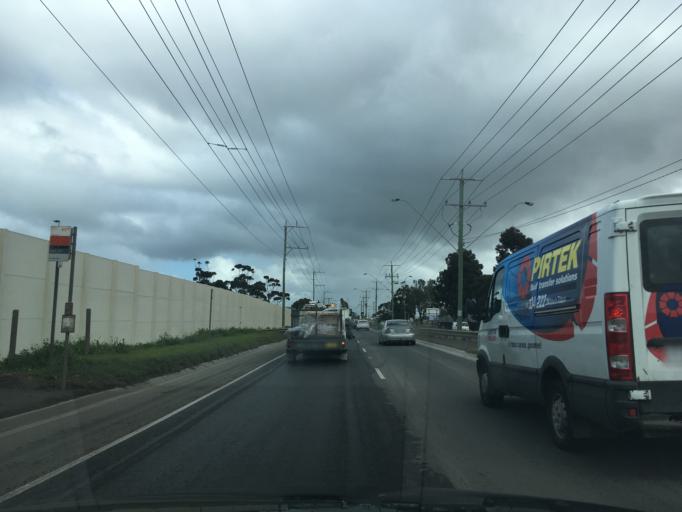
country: AU
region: Victoria
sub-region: Hobsons Bay
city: Laverton
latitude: -37.8342
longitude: 144.7842
